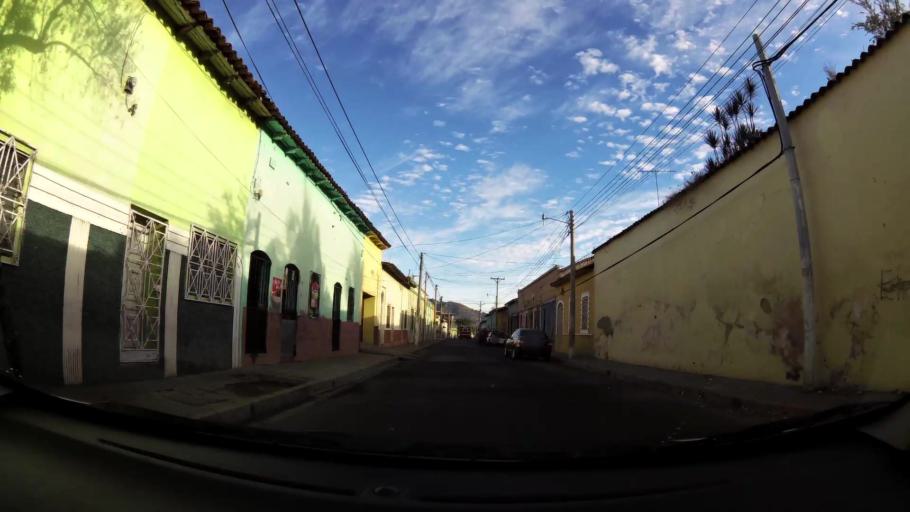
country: SV
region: Santa Ana
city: Santa Ana
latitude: 13.9946
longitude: -89.5526
